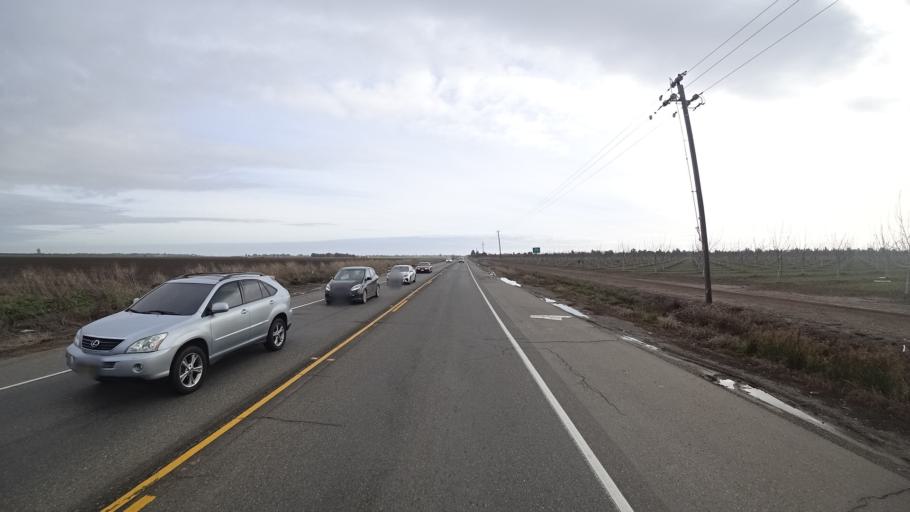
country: US
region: California
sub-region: Yolo County
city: Davis
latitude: 38.5616
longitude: -121.8029
